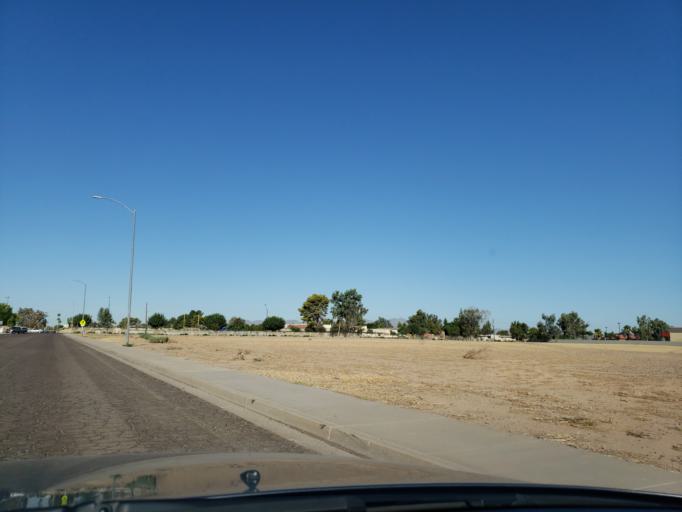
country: US
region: Arizona
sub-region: Maricopa County
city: Avondale
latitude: 33.4462
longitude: -112.3475
